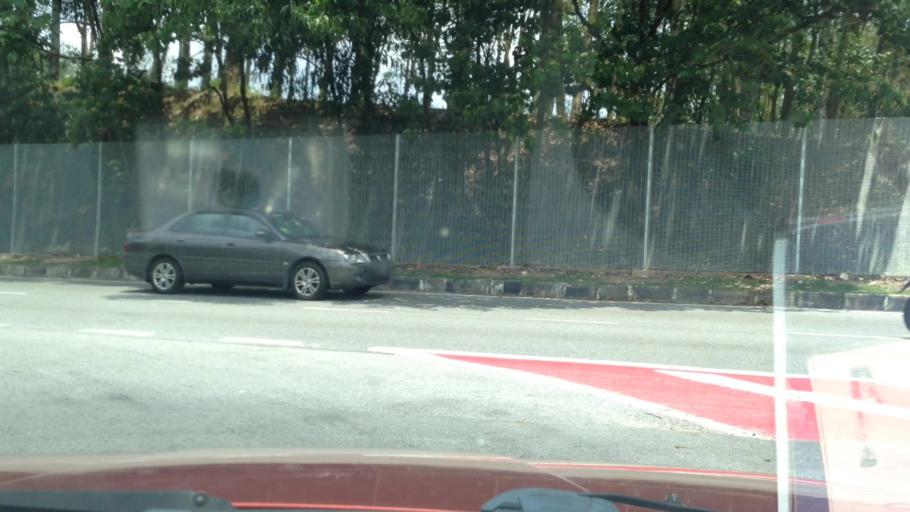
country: MY
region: Selangor
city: Kampung Baru Subang
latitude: 3.1659
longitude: 101.5518
